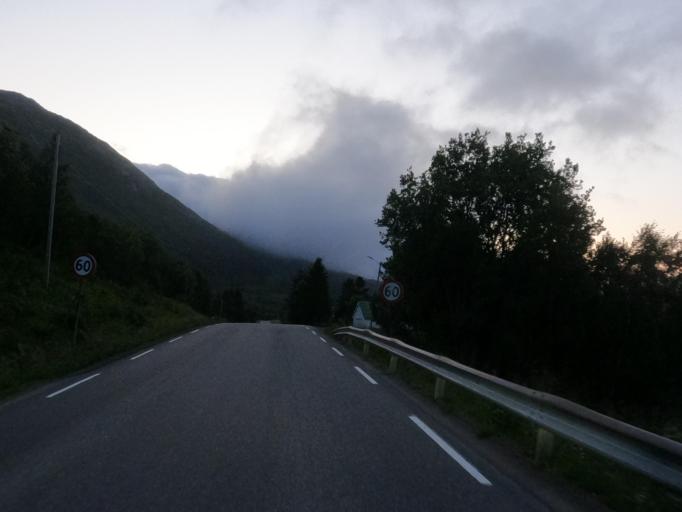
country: NO
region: Nordland
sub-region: Lodingen
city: Lodingen
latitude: 68.5663
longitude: 15.8010
